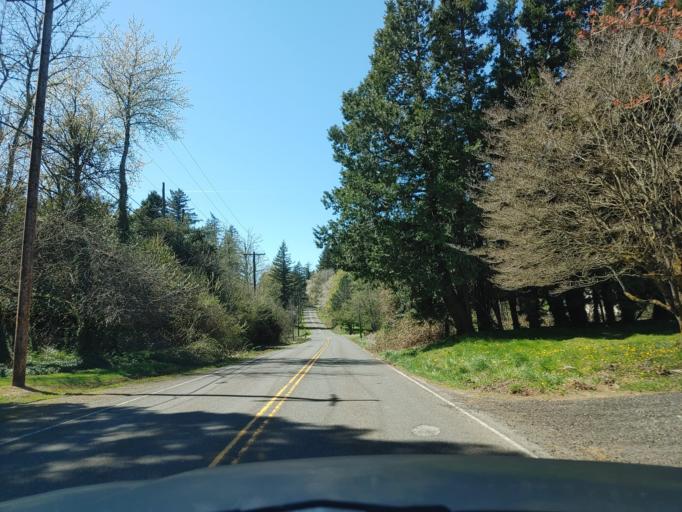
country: US
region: Oregon
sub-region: Multnomah County
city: Troutdale
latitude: 45.5191
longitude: -122.3417
